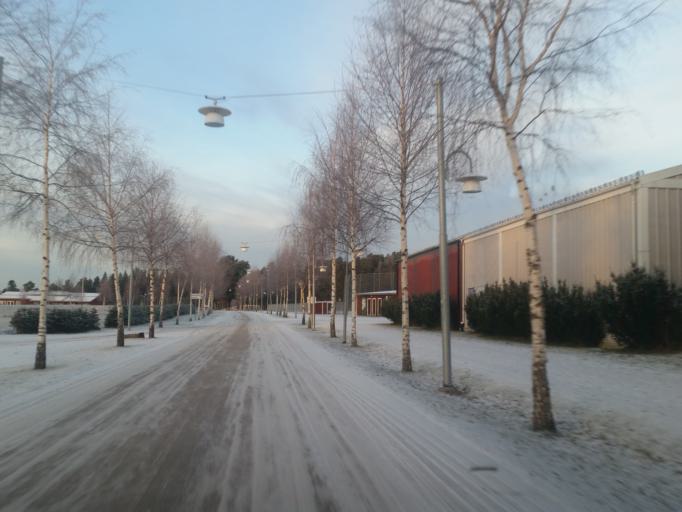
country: SE
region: Dalarna
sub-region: Leksand Municipality
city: Leksand
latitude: 60.7351
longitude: 14.9836
